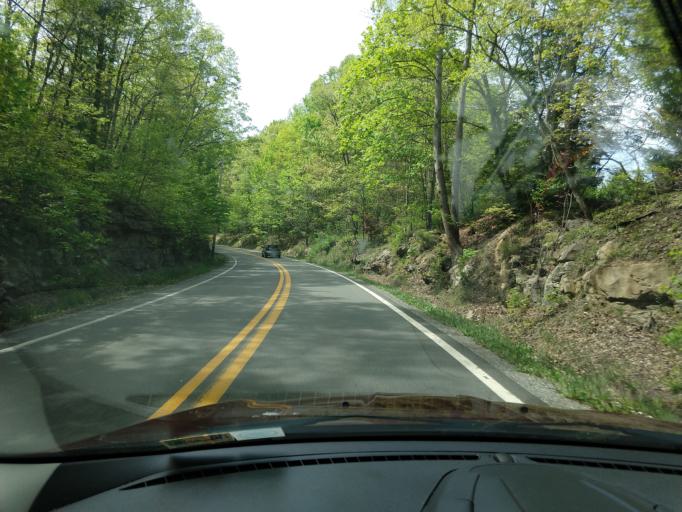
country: US
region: West Virginia
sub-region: Raleigh County
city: Daniels
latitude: 37.7844
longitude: -81.1140
